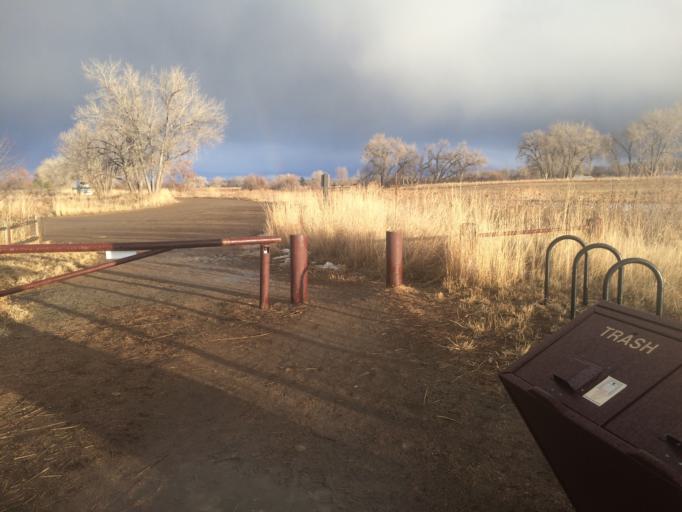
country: US
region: Colorado
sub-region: Boulder County
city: Gunbarrel
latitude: 40.0395
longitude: -105.1855
